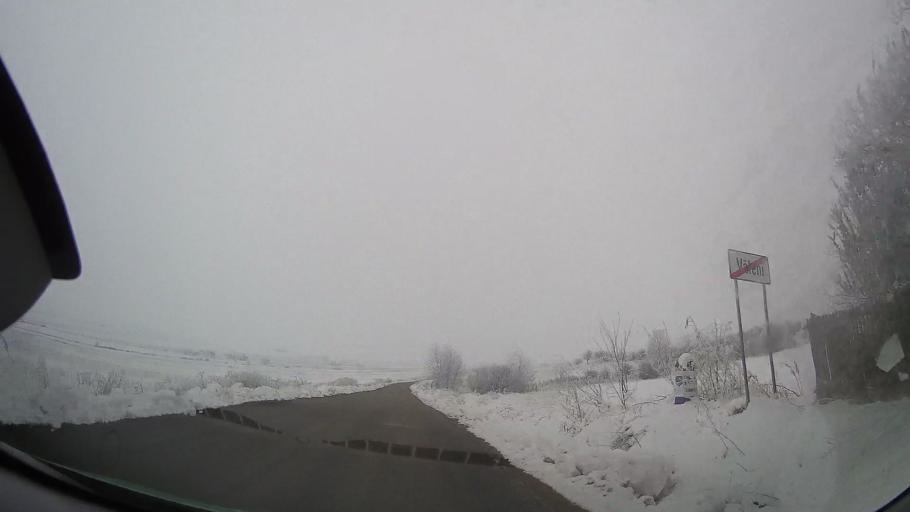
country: RO
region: Iasi
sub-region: Comuna Tansa
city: Suhulet
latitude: 46.8879
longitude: 27.2771
